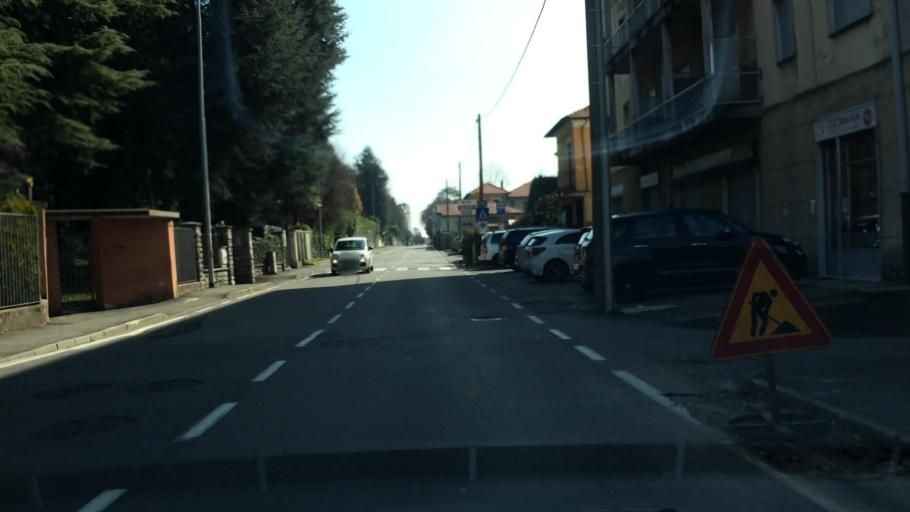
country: IT
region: Lombardy
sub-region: Provincia di Como
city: Lomazzo
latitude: 45.6992
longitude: 9.0273
